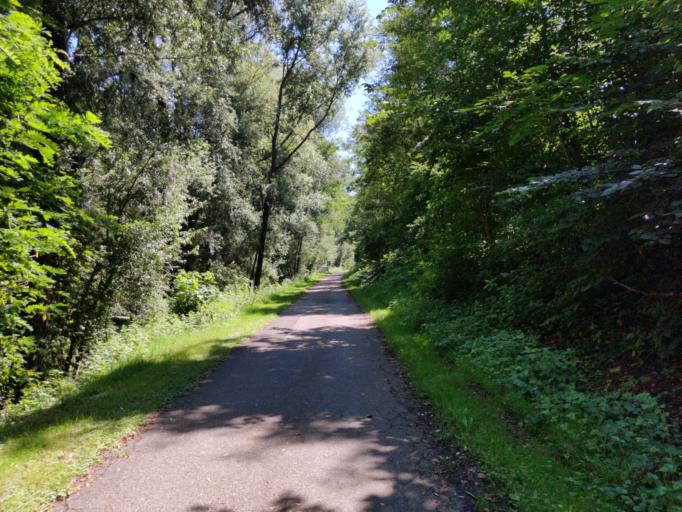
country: AT
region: Styria
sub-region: Politischer Bezirk Leibnitz
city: Sankt Veit am Vogau
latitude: 46.7248
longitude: 15.6039
